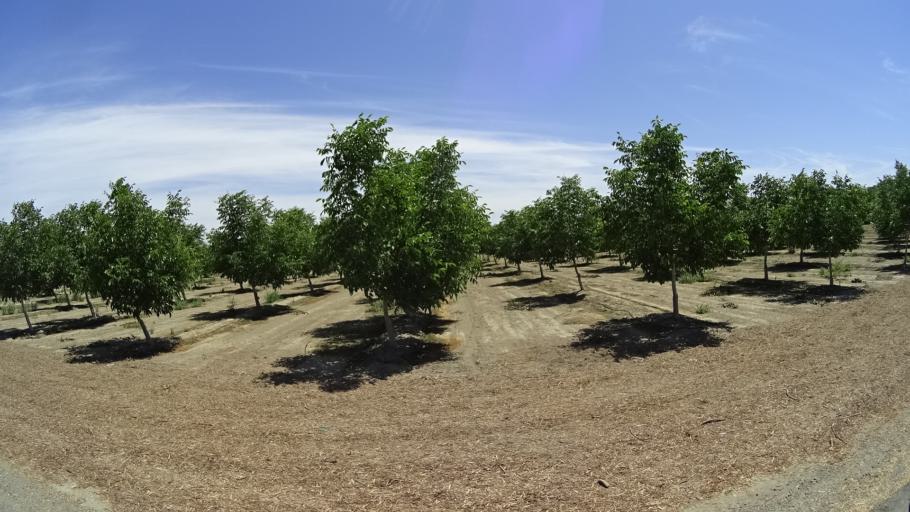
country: US
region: California
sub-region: Kings County
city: Lemoore
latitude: 36.3435
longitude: -119.7673
